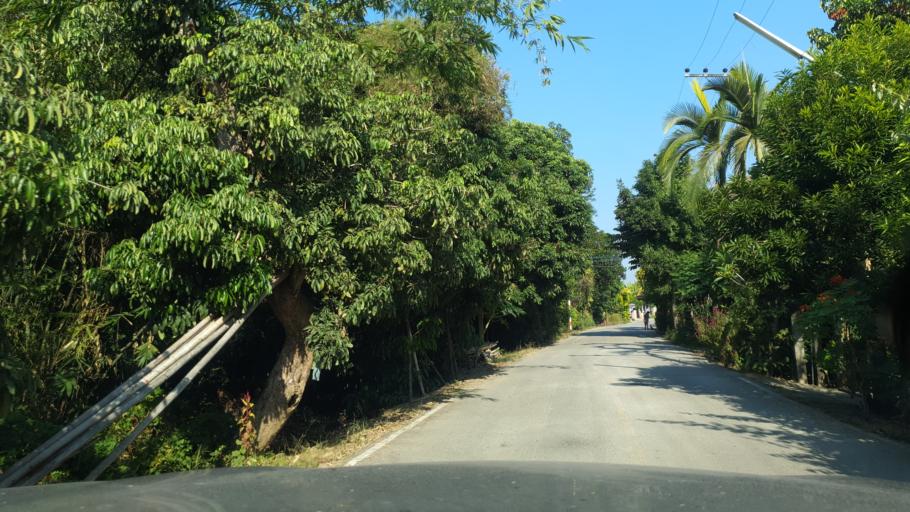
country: TH
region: Chiang Mai
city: Saraphi
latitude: 18.6997
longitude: 99.0773
